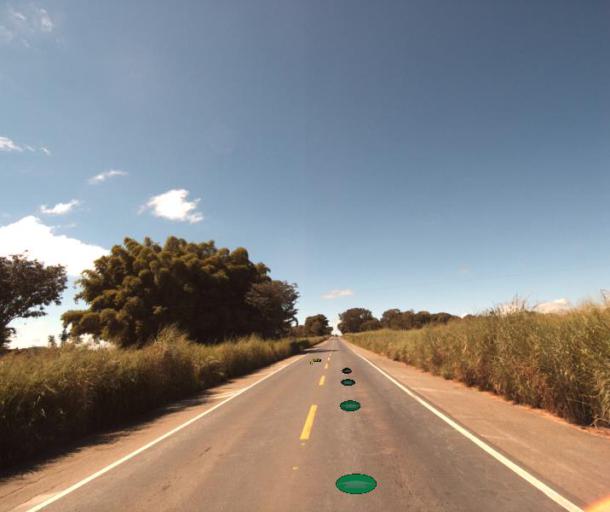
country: BR
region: Goias
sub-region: Jaragua
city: Jaragua
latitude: -15.5567
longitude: -49.4263
